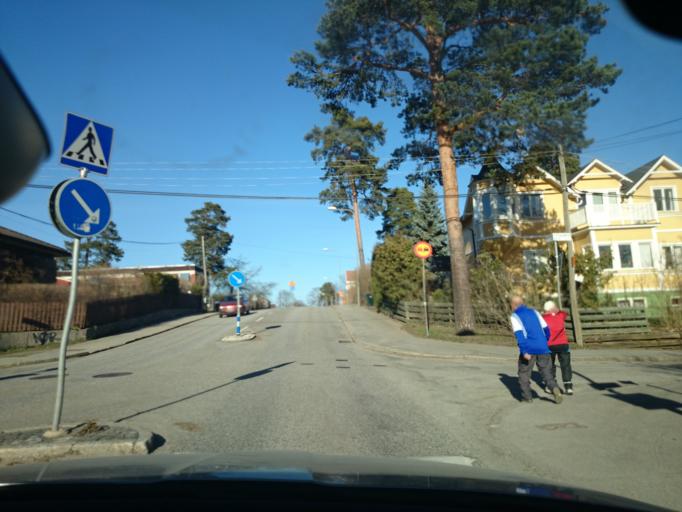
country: SE
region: Stockholm
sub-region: Huddinge Kommun
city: Huddinge
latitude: 59.2750
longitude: 17.9914
